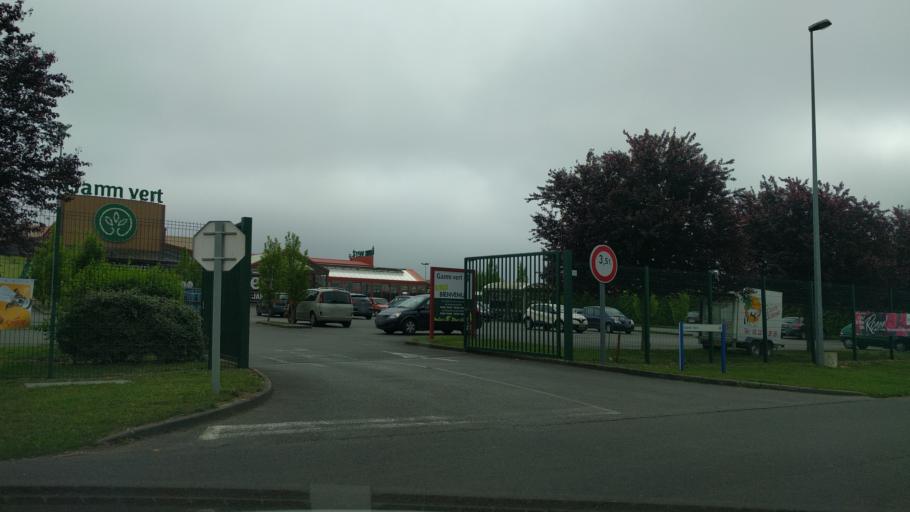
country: FR
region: Picardie
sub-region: Departement de la Somme
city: Peronne
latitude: 49.9409
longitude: 2.9262
